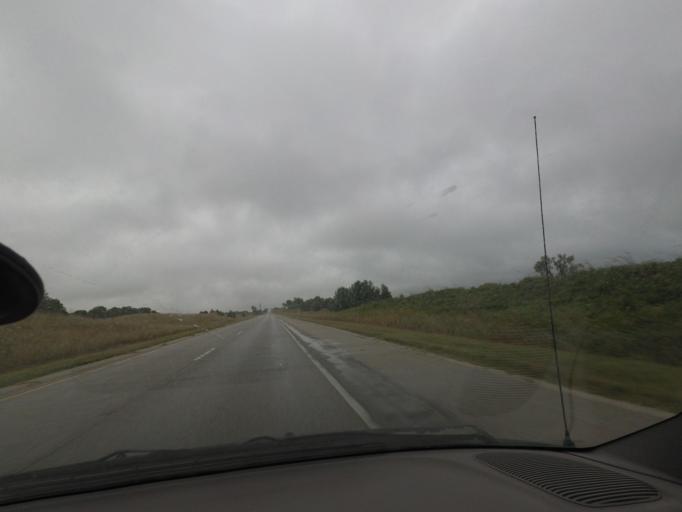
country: US
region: Illinois
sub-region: Pike County
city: Barry
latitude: 39.7322
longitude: -91.1241
